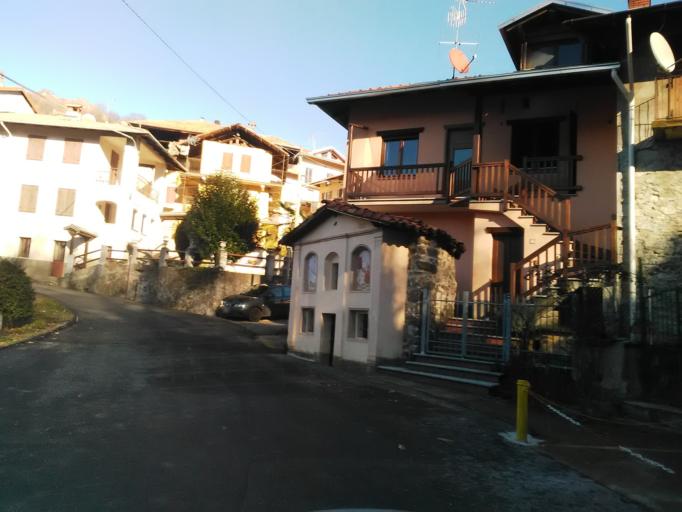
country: IT
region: Piedmont
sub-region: Provincia di Biella
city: Coggiola
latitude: 45.6960
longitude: 8.1797
